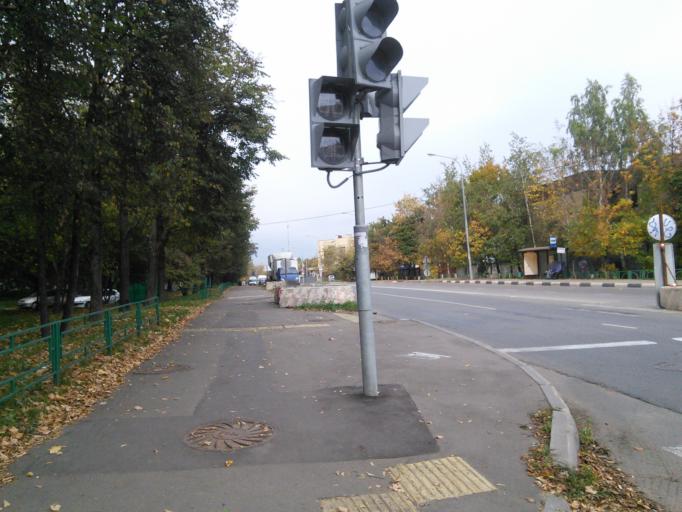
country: RU
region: Moskovskaya
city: Levoberezhnaya
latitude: 55.8716
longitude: 37.4705
